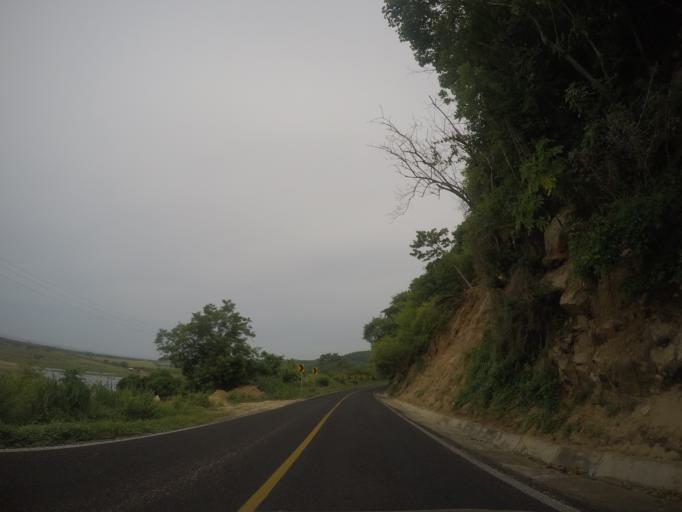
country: MX
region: Oaxaca
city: San Pedro Mixtepec
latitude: 15.9505
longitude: -97.2590
